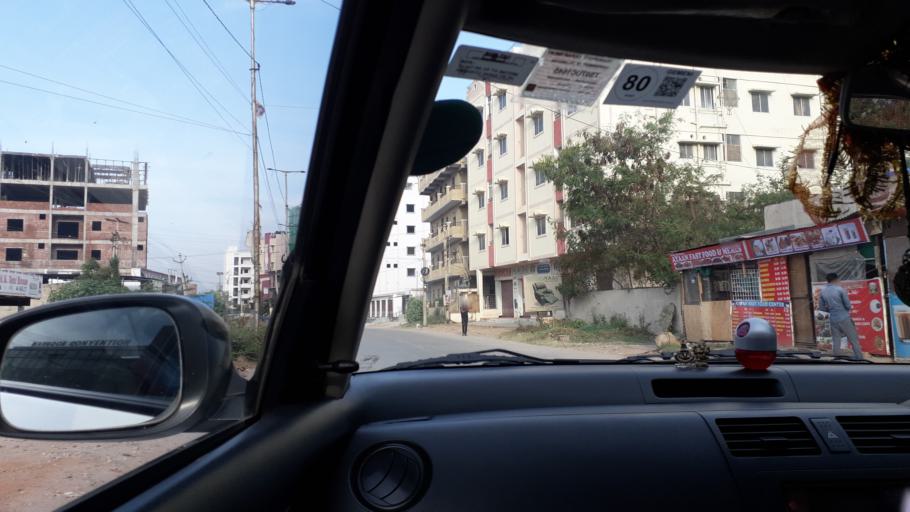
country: IN
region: Telangana
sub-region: Hyderabad
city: Hyderabad
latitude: 17.3945
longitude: 78.3852
